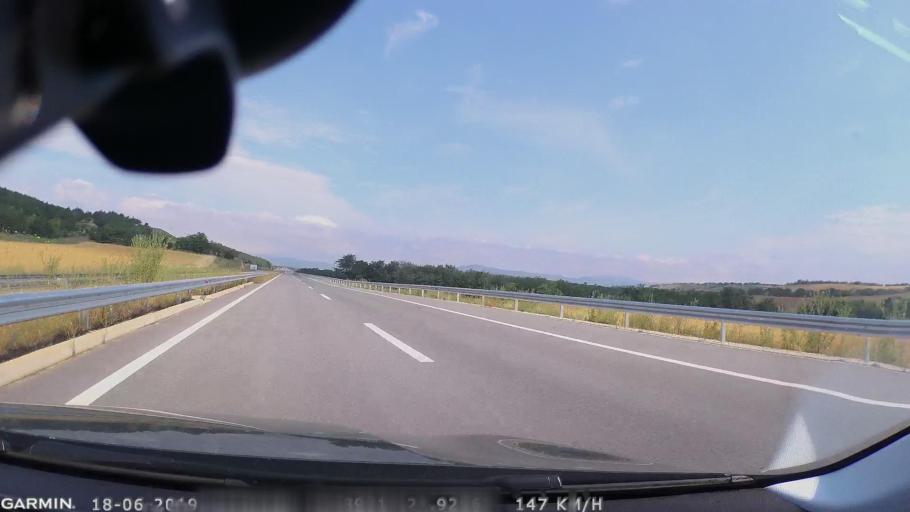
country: MK
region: Sveti Nikole
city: Sveti Nikole
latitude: 41.8939
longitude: 21.9247
